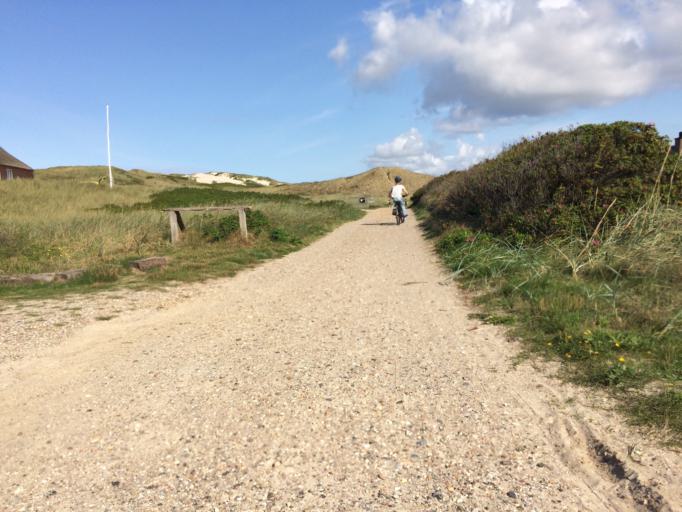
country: DK
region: Central Jutland
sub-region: Ringkobing-Skjern Kommune
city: Hvide Sande
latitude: 55.9286
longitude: 8.1509
